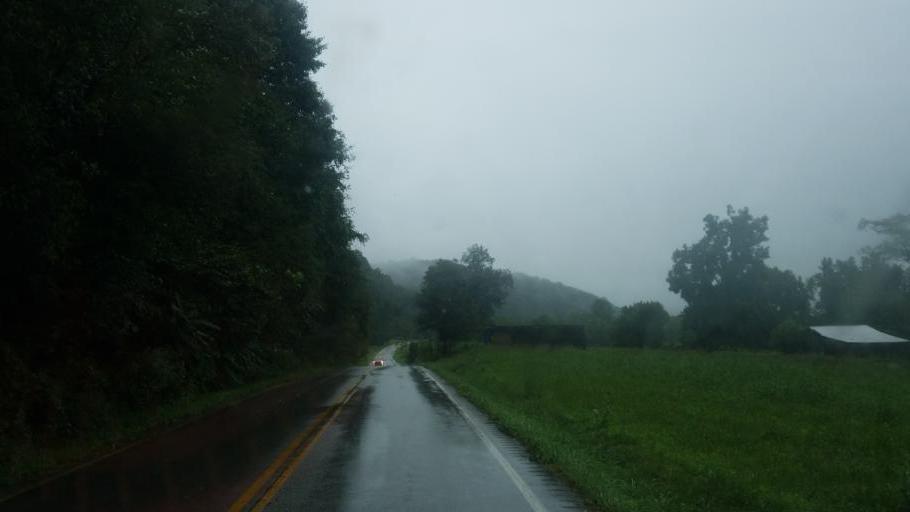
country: US
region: Kentucky
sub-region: Greenup County
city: South Shore
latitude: 38.6905
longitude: -82.9378
